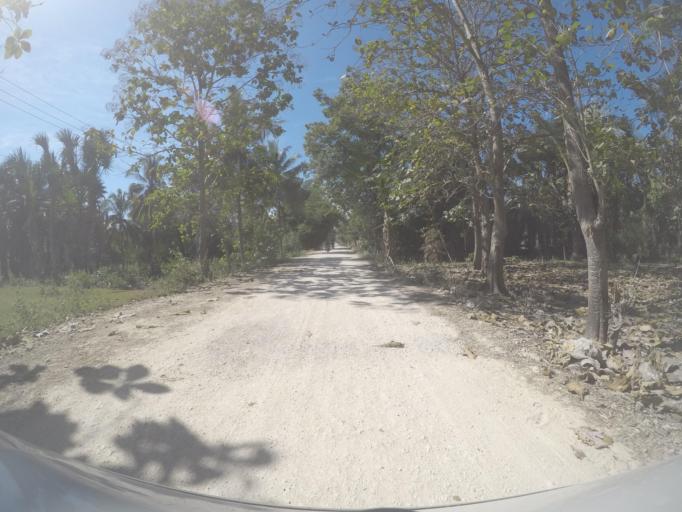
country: TL
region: Viqueque
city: Viqueque
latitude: -8.8957
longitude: 126.5064
